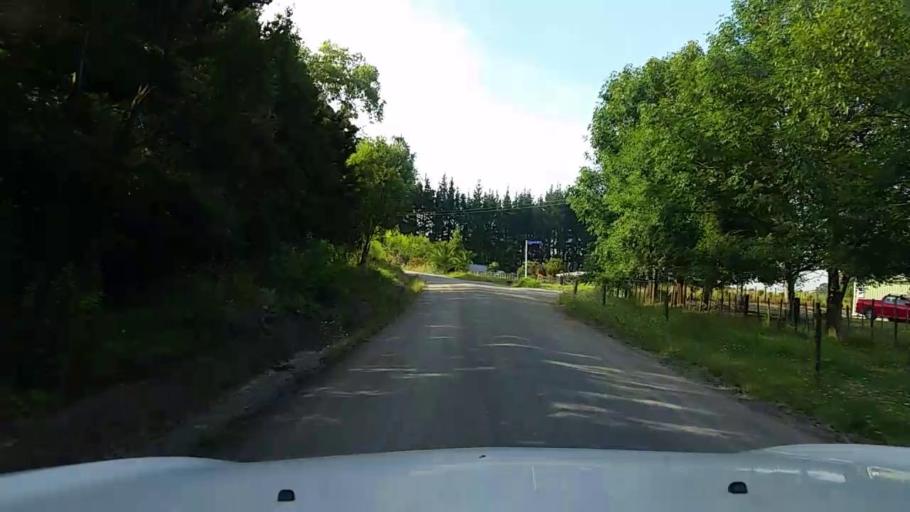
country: NZ
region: Northland
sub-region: Whangarei
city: Maungatapere
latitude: -35.6792
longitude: 174.1785
